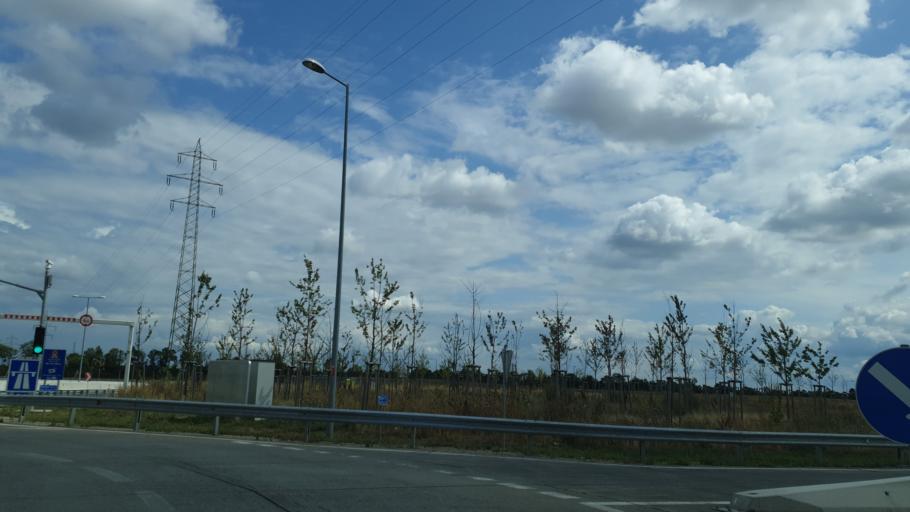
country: AT
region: Lower Austria
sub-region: Politischer Bezirk Modling
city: Hennersdorf
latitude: 48.1288
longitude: 16.3713
